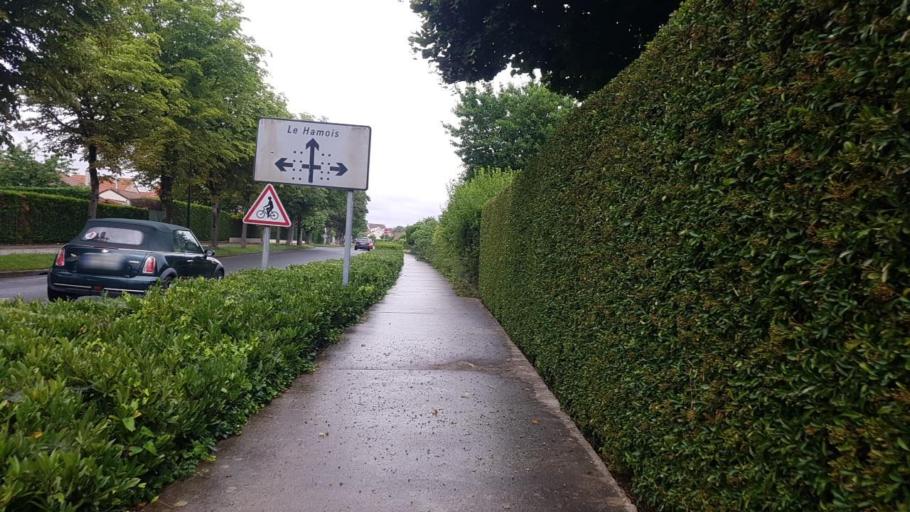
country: FR
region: Champagne-Ardenne
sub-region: Departement de la Marne
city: Vitry-le-Francois
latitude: 48.7330
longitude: 4.5980
